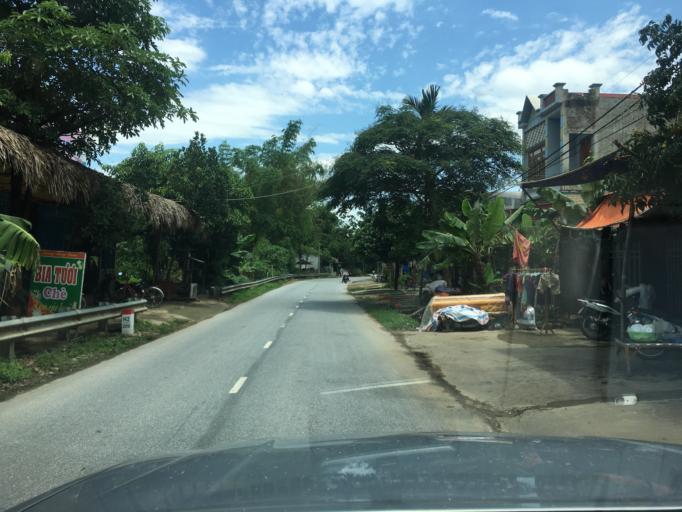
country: VN
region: Yen Bai
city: Son Thinh
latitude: 21.6539
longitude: 104.5009
